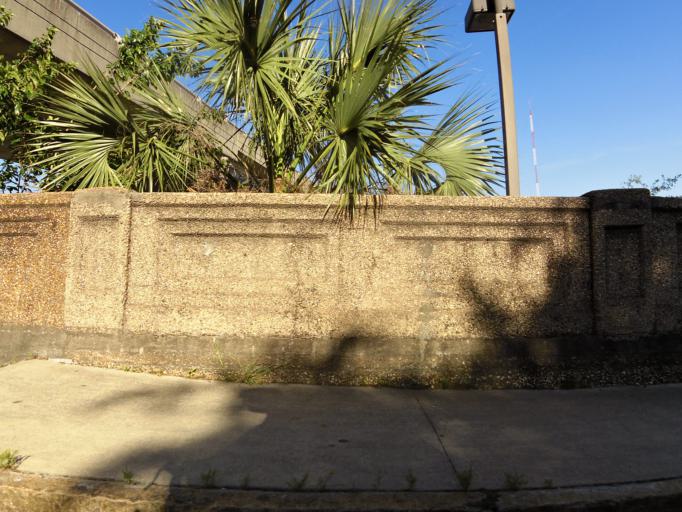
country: US
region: Florida
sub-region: Duval County
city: Jacksonville
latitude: 30.3273
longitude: -81.6496
